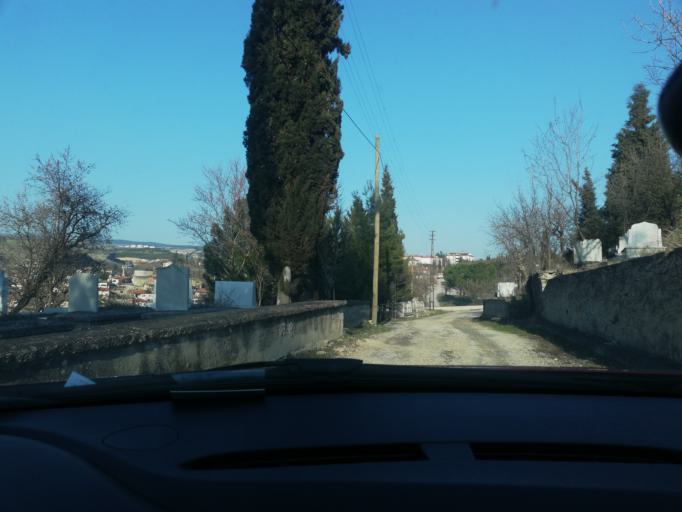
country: TR
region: Karabuk
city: Safranbolu
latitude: 41.2407
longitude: 32.6916
